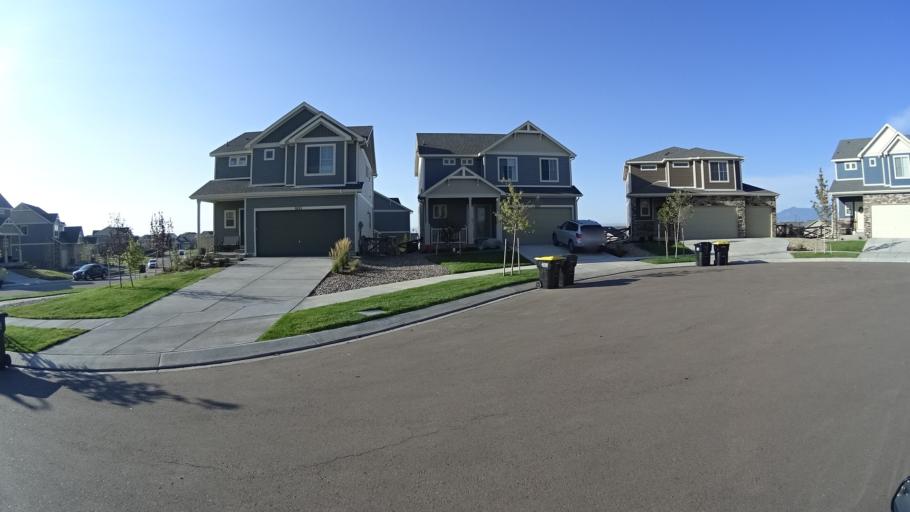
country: US
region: Colorado
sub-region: El Paso County
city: Cimarron Hills
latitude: 38.9304
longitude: -104.6573
